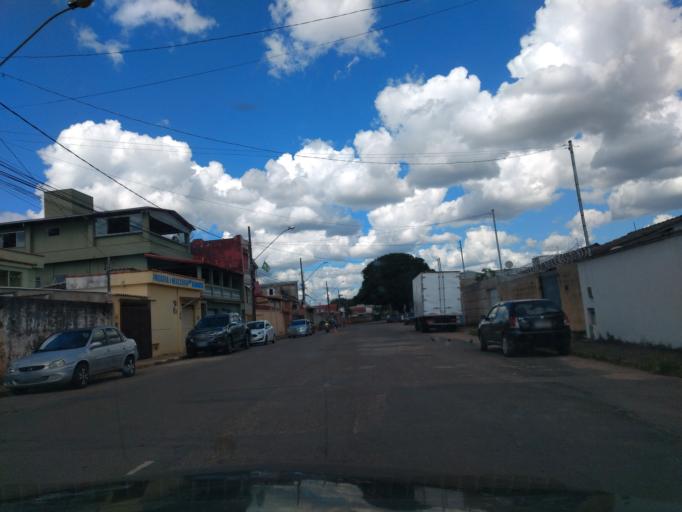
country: BR
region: Minas Gerais
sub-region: Tres Coracoes
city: Tres Coracoes
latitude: -21.6851
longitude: -45.2662
